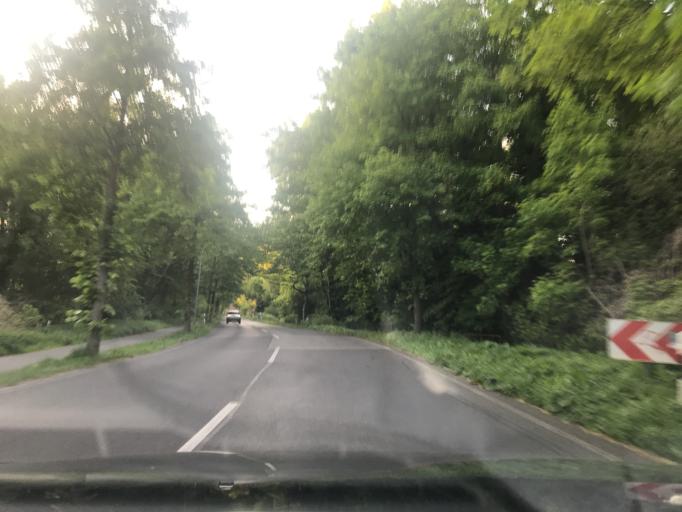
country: DE
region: North Rhine-Westphalia
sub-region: Regierungsbezirk Dusseldorf
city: Korschenbroich
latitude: 51.2469
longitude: 6.4800
